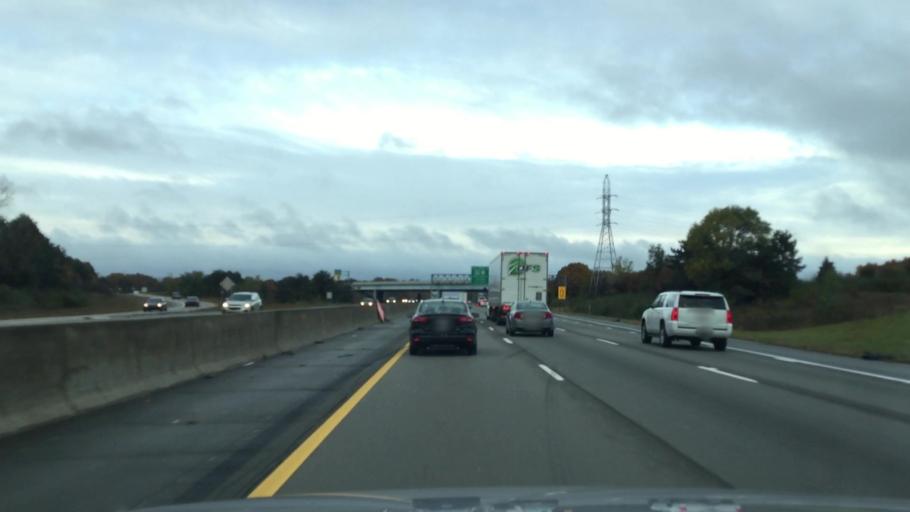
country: US
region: Michigan
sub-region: Washtenaw County
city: Ypsilanti
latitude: 42.2243
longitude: -83.6471
